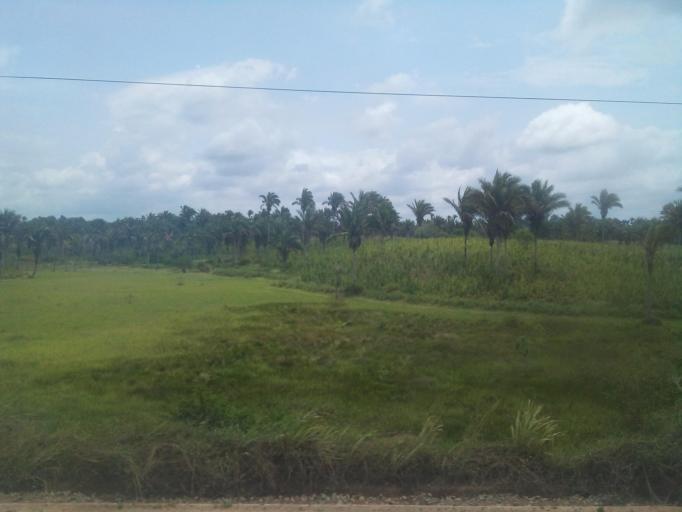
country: BR
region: Maranhao
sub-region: Santa Ines
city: Santa Ines
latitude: -3.6962
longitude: -45.6163
